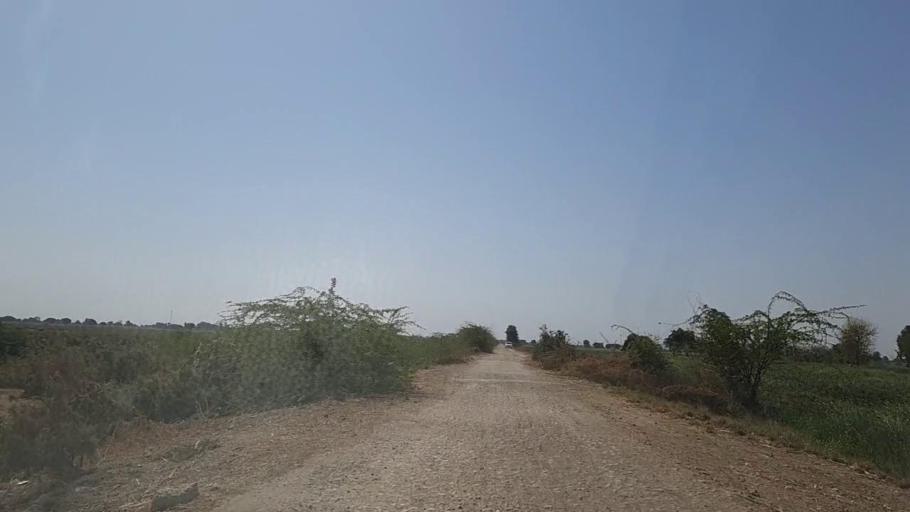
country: PK
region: Sindh
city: Samaro
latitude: 25.2364
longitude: 69.4100
